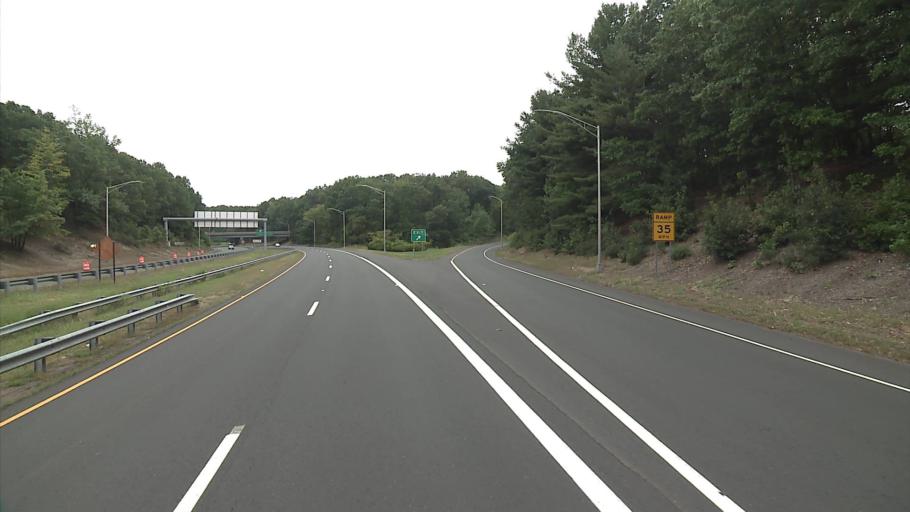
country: US
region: Connecticut
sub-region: Hartford County
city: Tariffville
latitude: 41.9265
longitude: -72.6962
